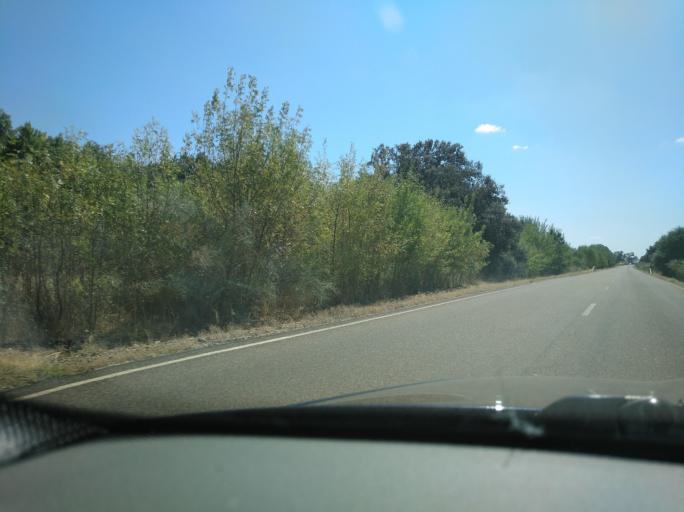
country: ES
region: Extremadura
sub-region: Provincia de Badajoz
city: Olivenza
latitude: 38.7175
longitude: -7.1994
